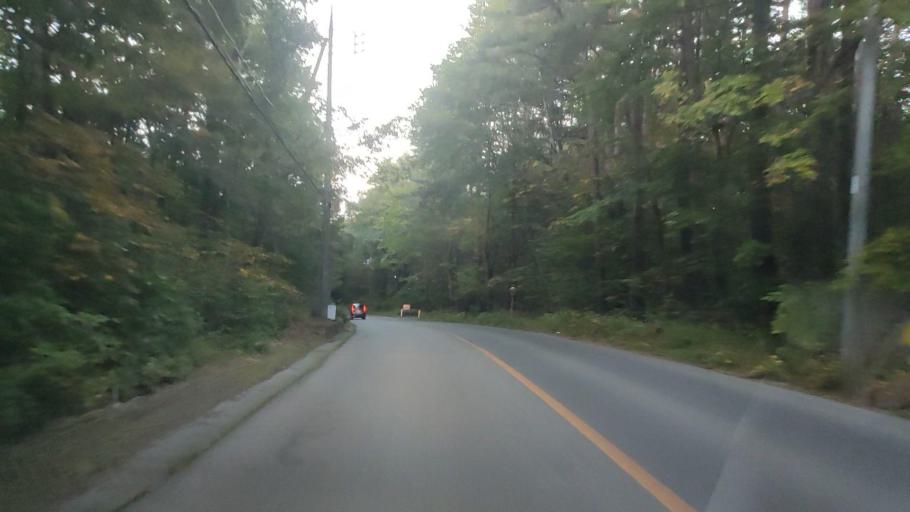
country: JP
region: Nagano
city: Komoro
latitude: 36.4490
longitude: 138.5814
